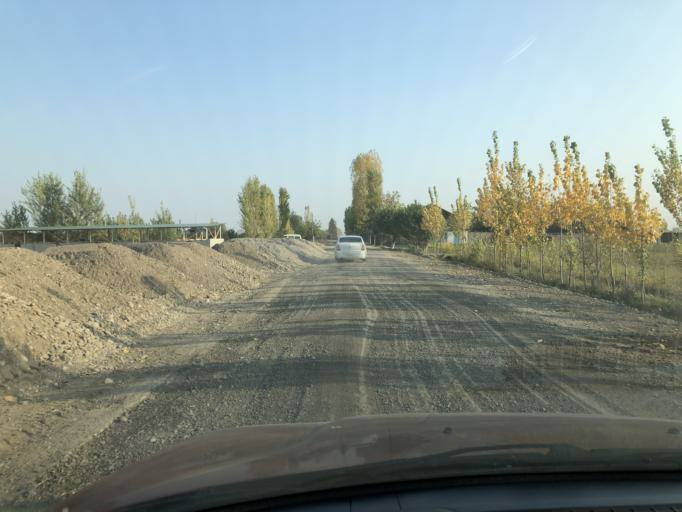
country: UZ
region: Namangan
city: Uychi
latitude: 41.0664
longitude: 71.9855
